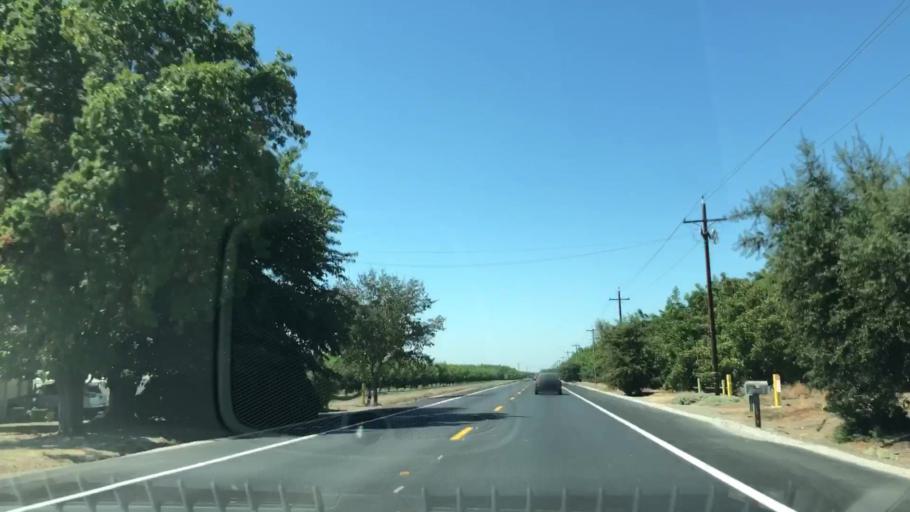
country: US
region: California
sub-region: San Joaquin County
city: Garden Acres
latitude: 37.9422
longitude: -121.1391
